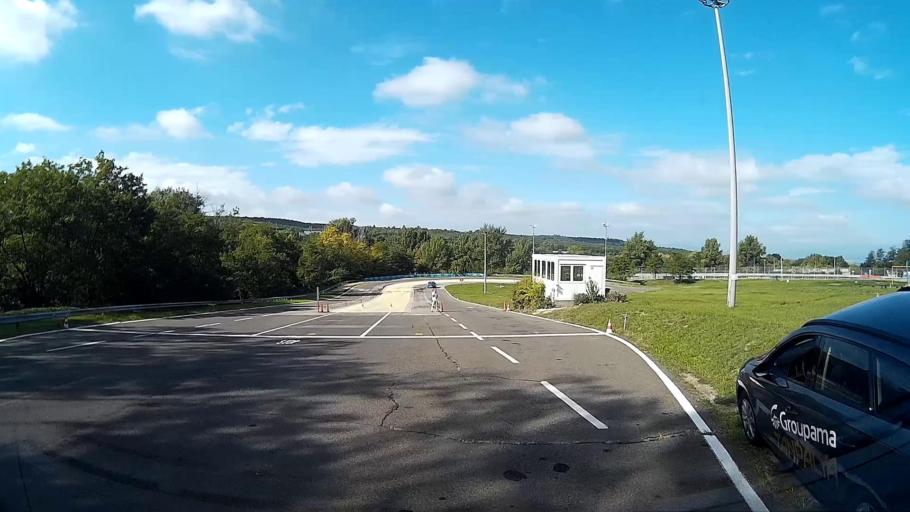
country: HU
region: Pest
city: Mogyorod
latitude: 47.5851
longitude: 19.2522
